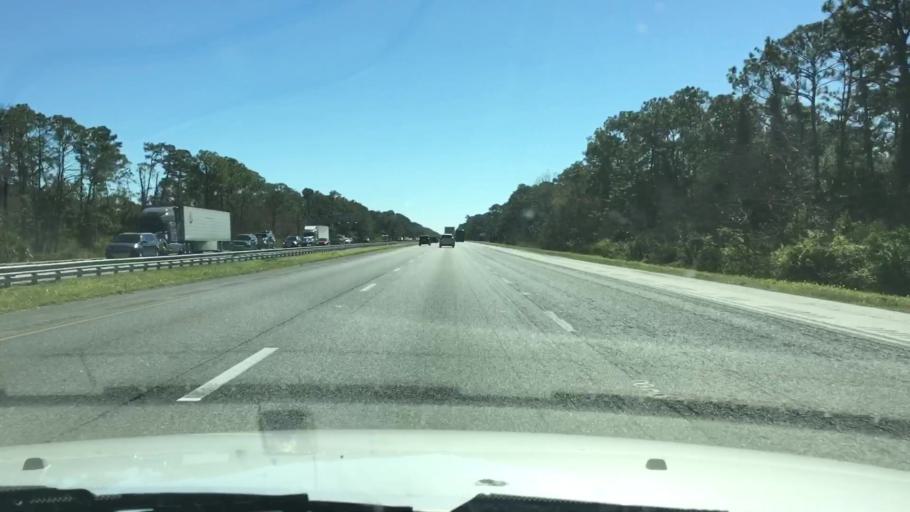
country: US
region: Florida
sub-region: Volusia County
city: Ormond-by-the-Sea
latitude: 29.3859
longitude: -81.1475
